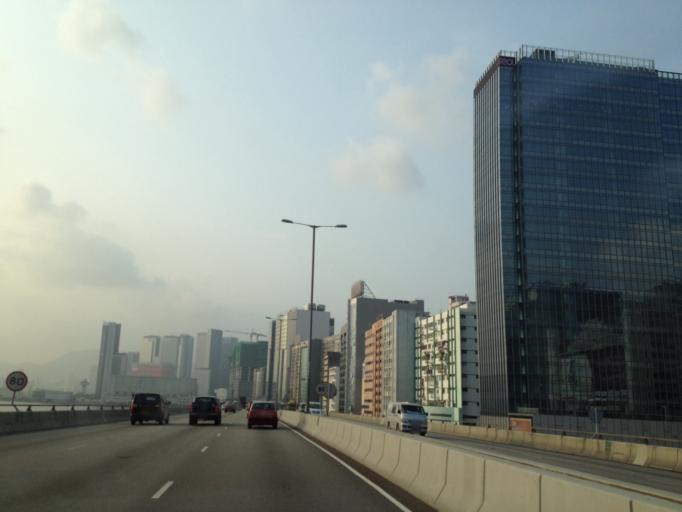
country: HK
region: Kowloon City
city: Kowloon
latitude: 22.3079
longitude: 114.2209
